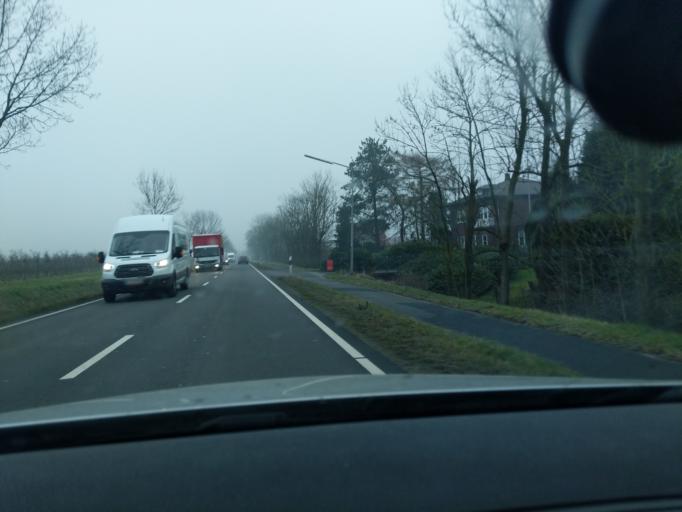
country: DE
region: Lower Saxony
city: Jork
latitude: 53.5462
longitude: 9.6731
